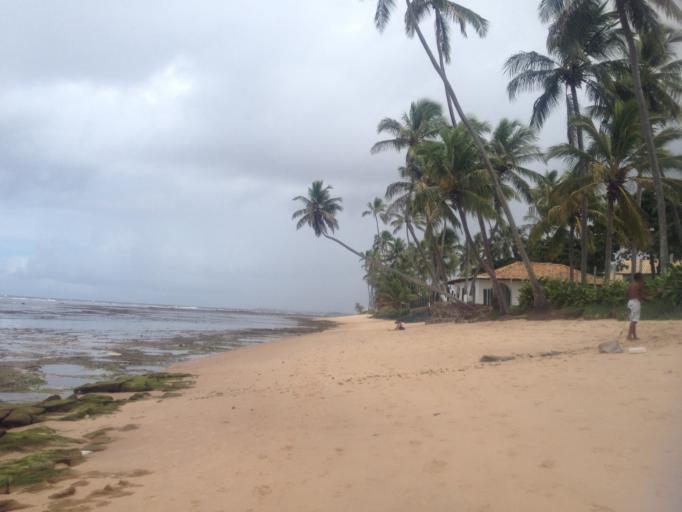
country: BR
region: Bahia
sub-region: Mata De Sao Joao
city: Mata de Sao Joao
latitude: -12.5787
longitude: -38.0042
